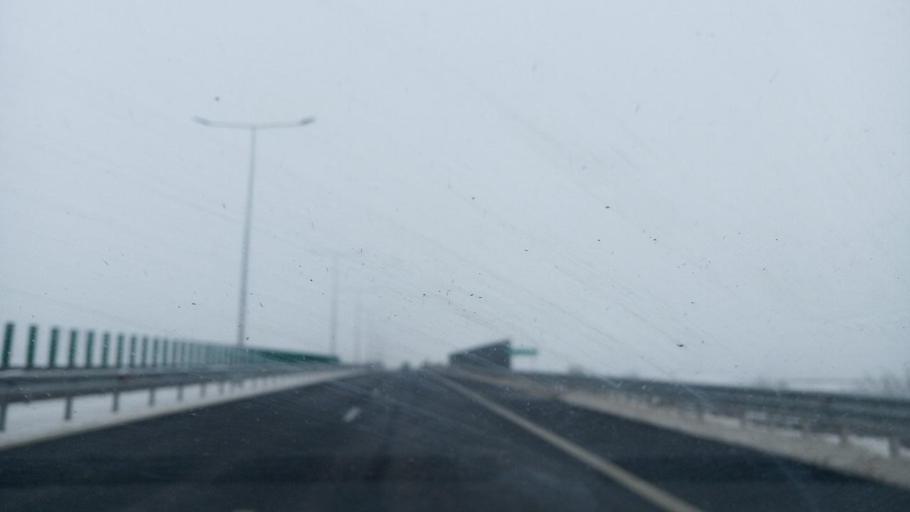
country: RO
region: Bacau
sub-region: Comuna Letea Veche
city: Holt
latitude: 46.6001
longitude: 26.9604
